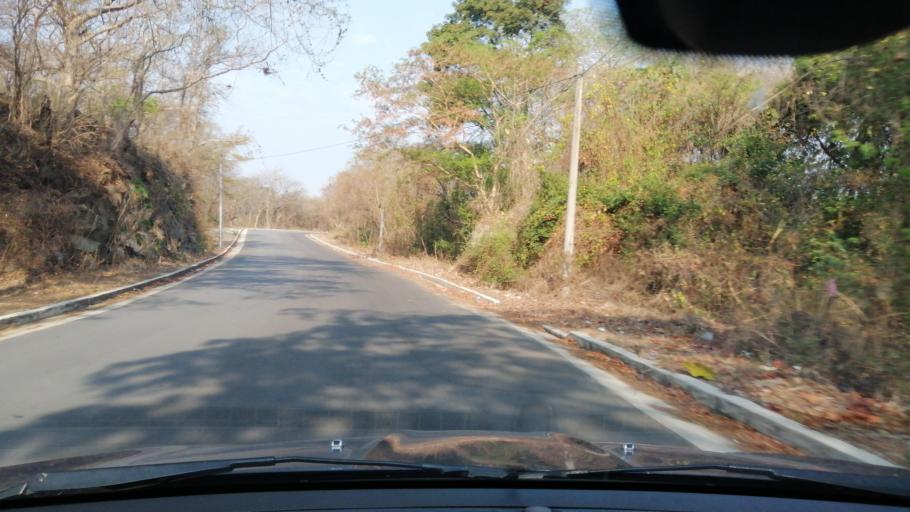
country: SV
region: Santa Ana
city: Metapan
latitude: 14.2315
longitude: -89.4590
